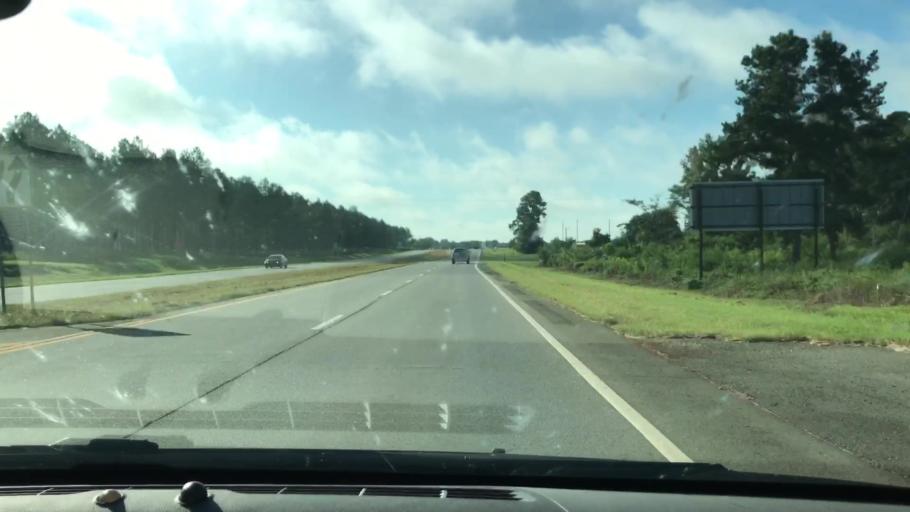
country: US
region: Georgia
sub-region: Terrell County
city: Dawson
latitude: 31.7502
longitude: -84.4219
